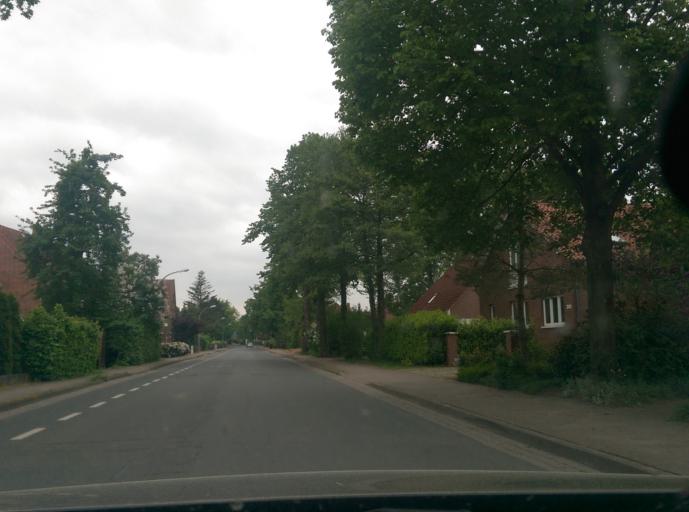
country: DE
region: Lower Saxony
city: Garbsen-Mitte
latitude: 52.4664
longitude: 9.6106
